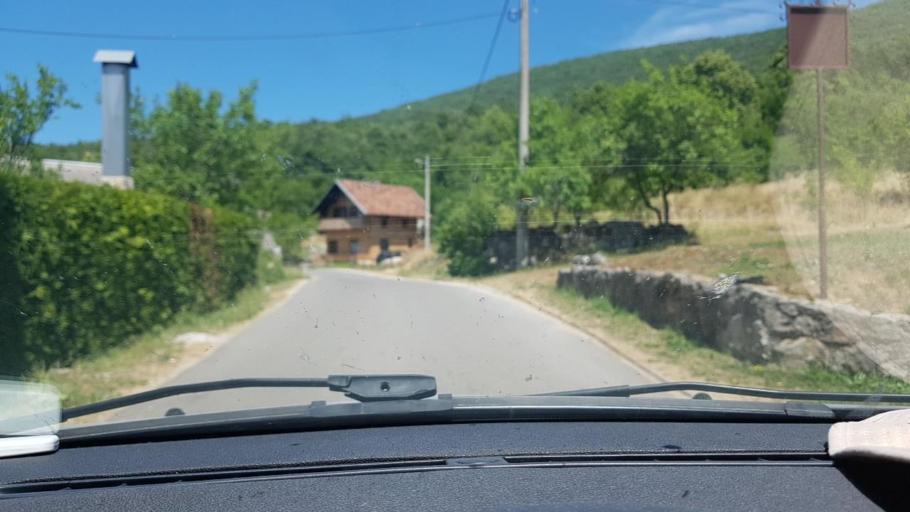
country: HR
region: Licko-Senjska
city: Otocac
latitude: 44.8144
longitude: 15.3592
